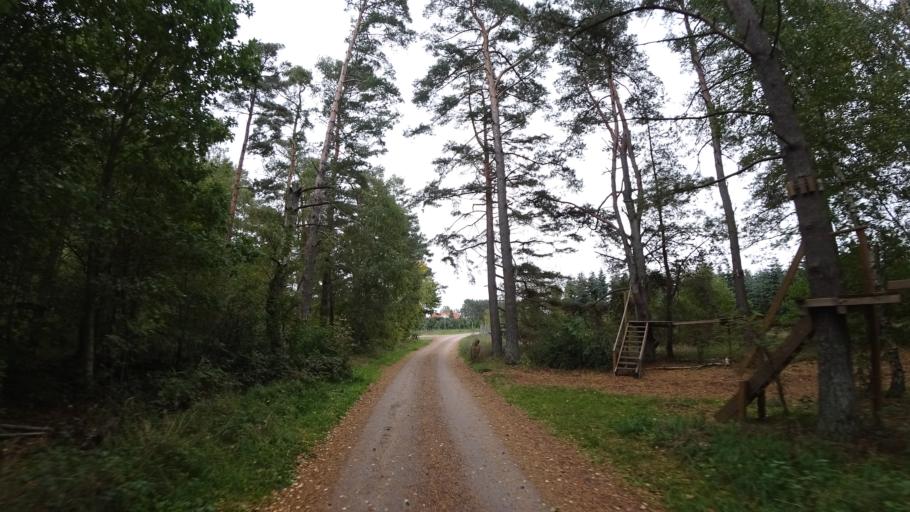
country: SE
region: Skane
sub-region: Kavlinge Kommun
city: Hofterup
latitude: 55.8204
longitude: 12.9671
